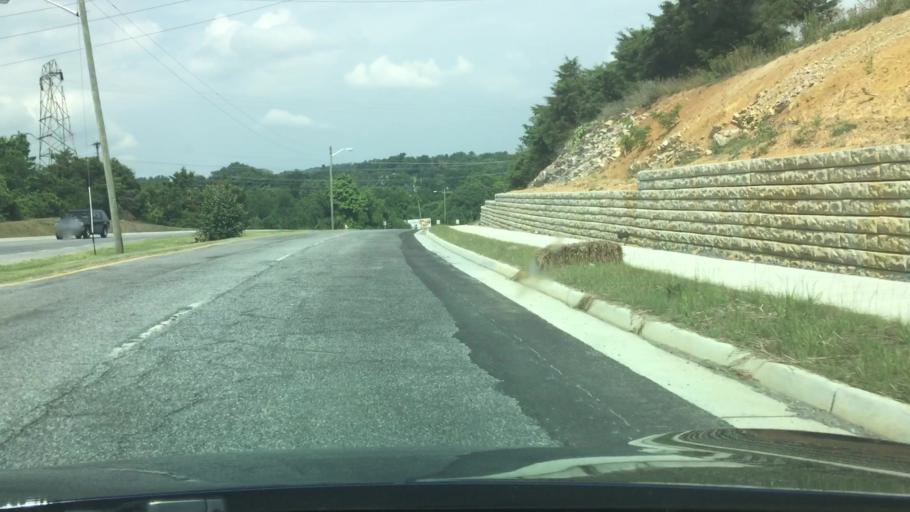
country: US
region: Virginia
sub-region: Wythe County
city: Wytheville
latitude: 36.9477
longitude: -81.0597
